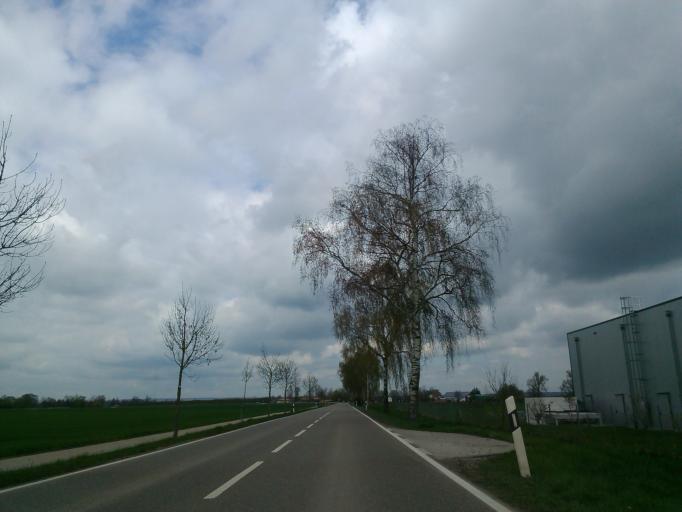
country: DE
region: Bavaria
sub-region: Swabia
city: Leipheim
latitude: 48.4596
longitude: 10.2091
